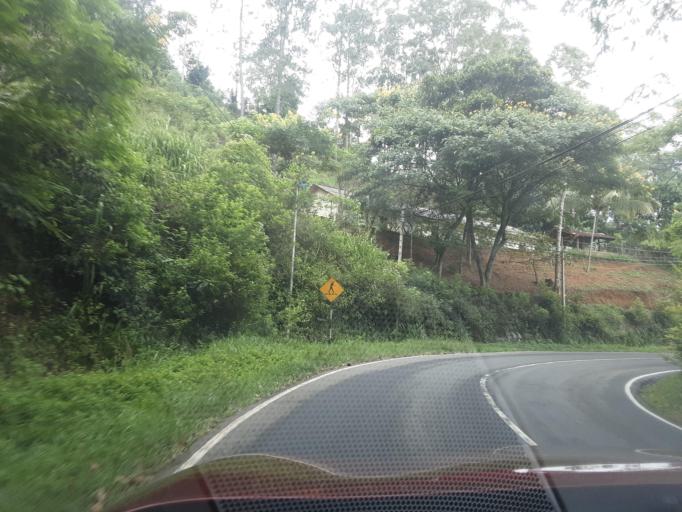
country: LK
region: Uva
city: Haputale
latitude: 6.8520
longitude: 80.9684
